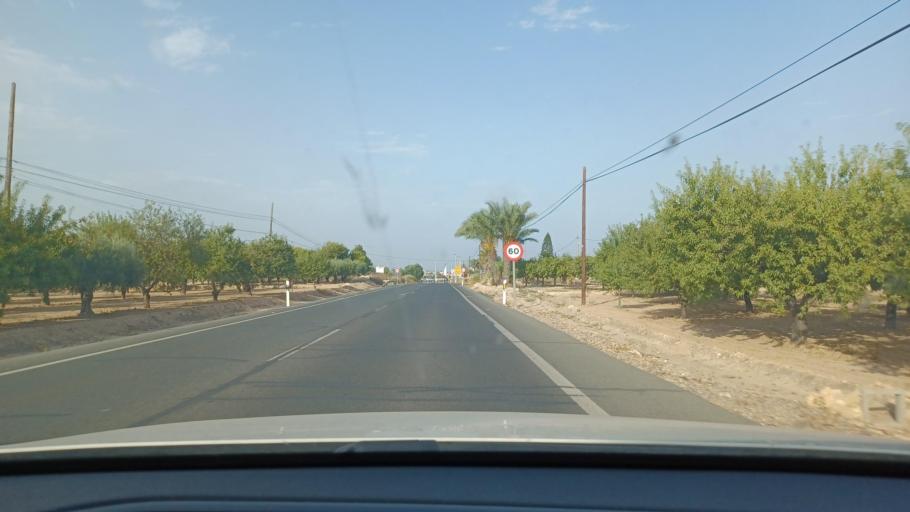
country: ES
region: Valencia
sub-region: Provincia de Alicante
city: Elche
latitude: 38.2834
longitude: -0.6275
